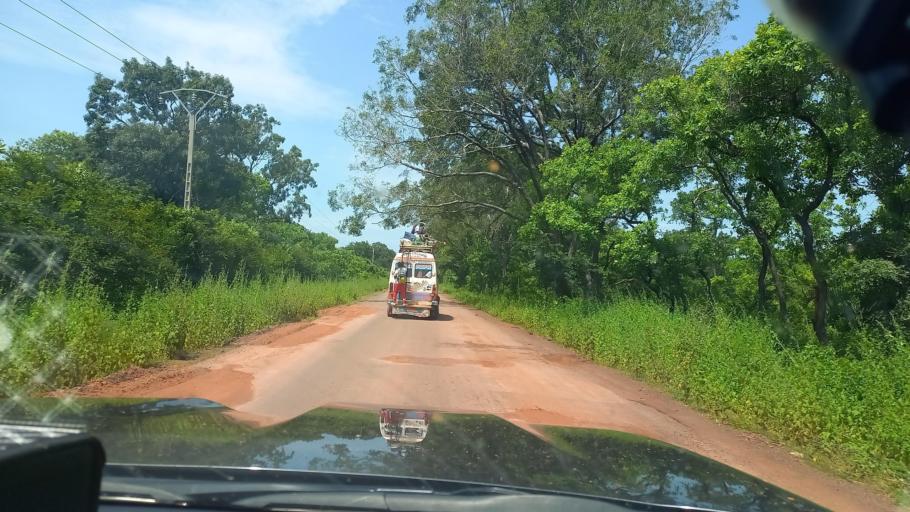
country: SN
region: Ziguinchor
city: Bignona
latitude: 12.8574
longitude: -16.1078
